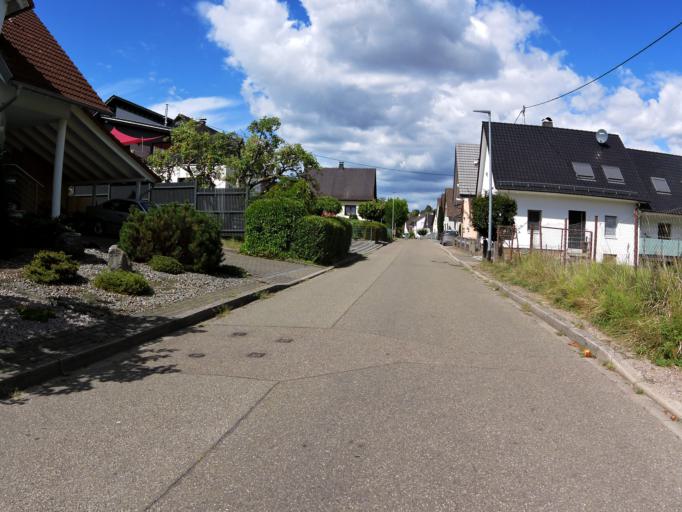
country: DE
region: Baden-Wuerttemberg
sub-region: Freiburg Region
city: Lahr
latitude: 48.3058
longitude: 7.8668
